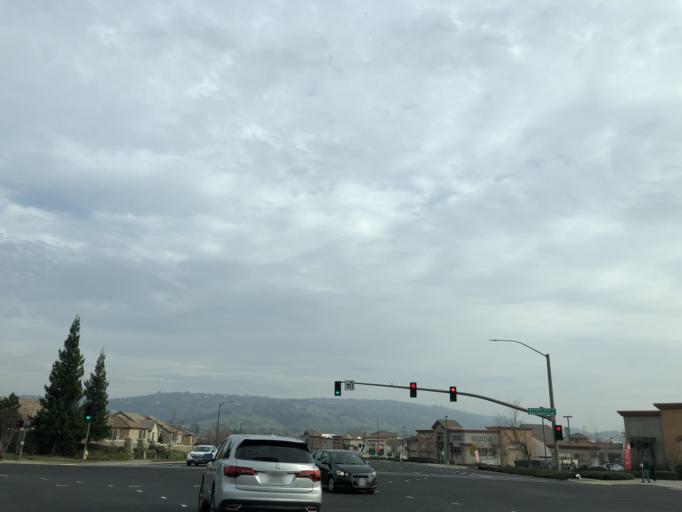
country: US
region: California
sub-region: El Dorado County
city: El Dorado Hills
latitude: 38.6909
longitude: -121.1235
